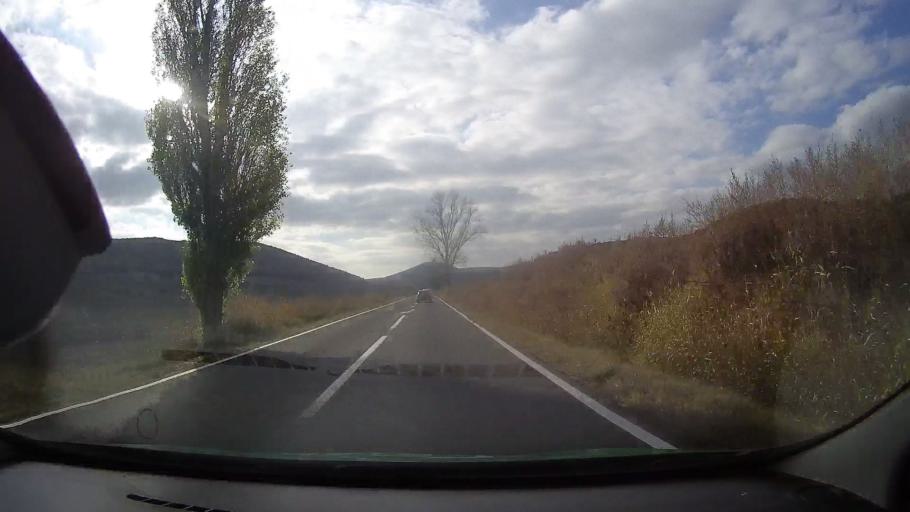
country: RO
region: Tulcea
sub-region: Comuna Nalbant
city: Nicolae Balcescu
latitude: 44.9682
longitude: 28.5353
